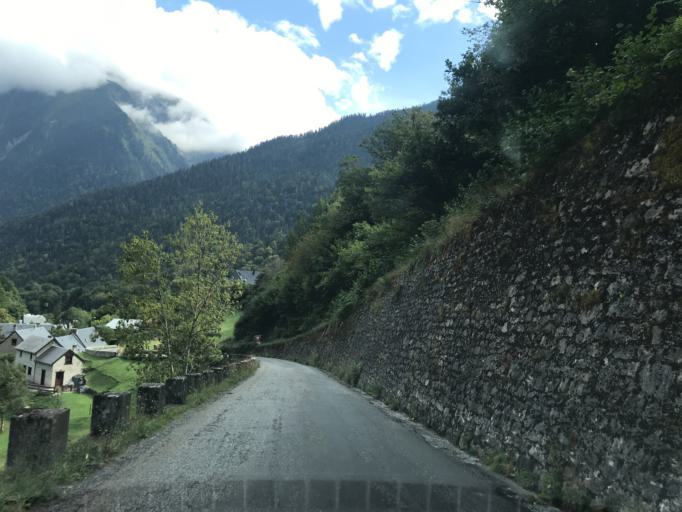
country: FR
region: Midi-Pyrenees
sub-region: Departement des Hautes-Pyrenees
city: Saint-Lary-Soulan
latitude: 42.7922
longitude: 0.2258
